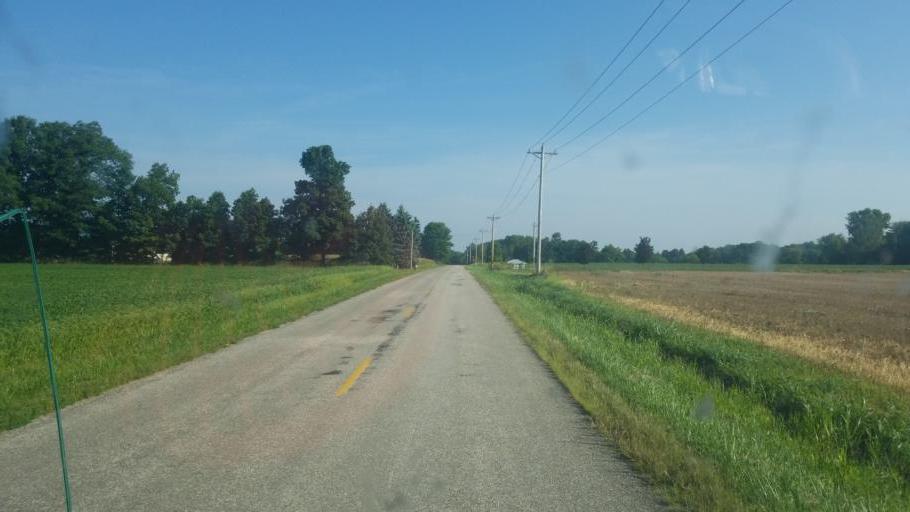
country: US
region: Ohio
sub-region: Huron County
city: New London
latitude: 41.0354
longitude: -82.3567
